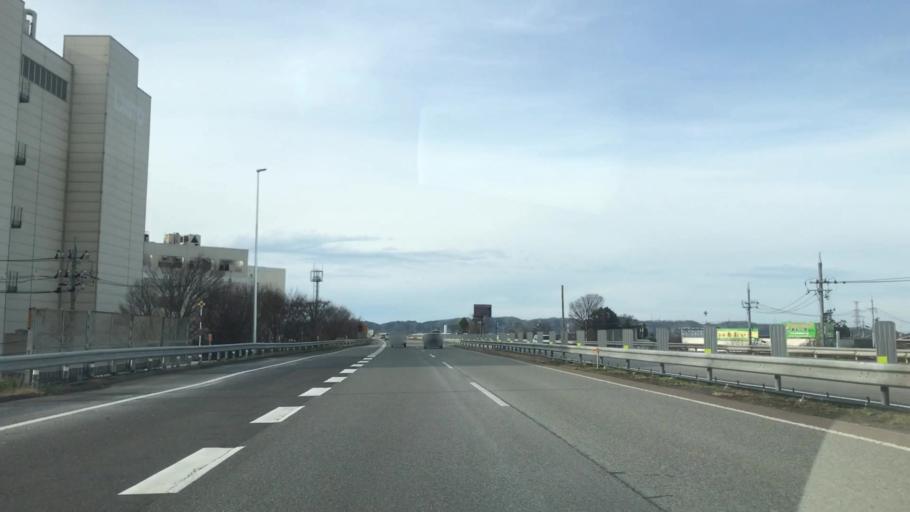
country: JP
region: Toyama
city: Toyama-shi
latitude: 36.6571
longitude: 137.2030
